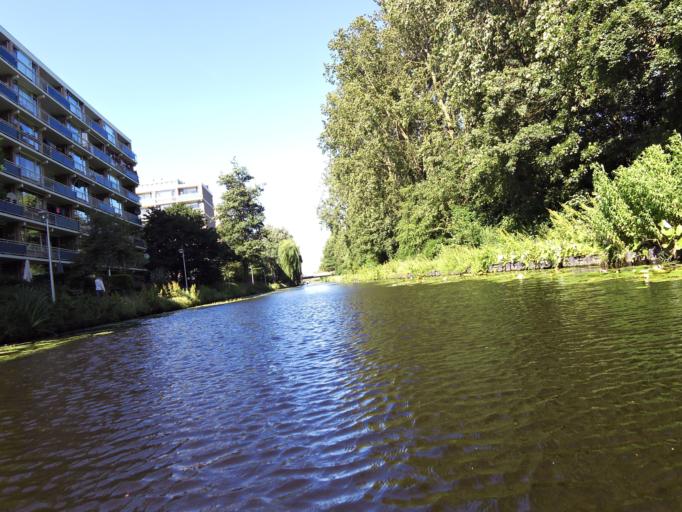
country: NL
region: South Holland
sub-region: Gemeente Wassenaar
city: Wassenaar
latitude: 52.1486
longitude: 4.4097
